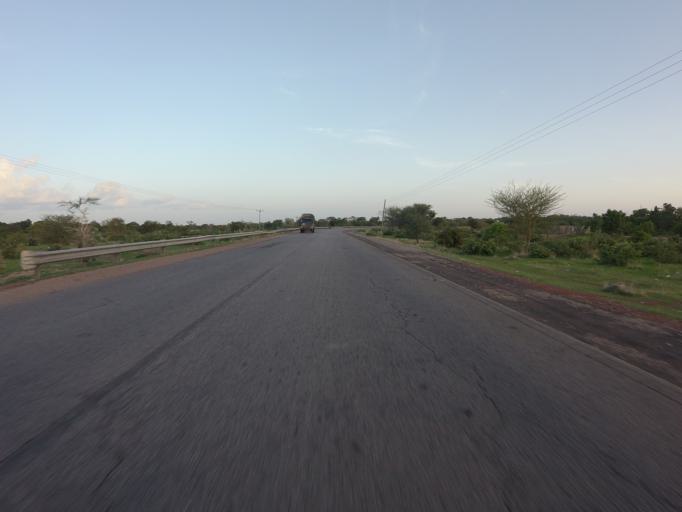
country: GH
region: Upper East
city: Navrongo
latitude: 10.9332
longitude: -1.0891
